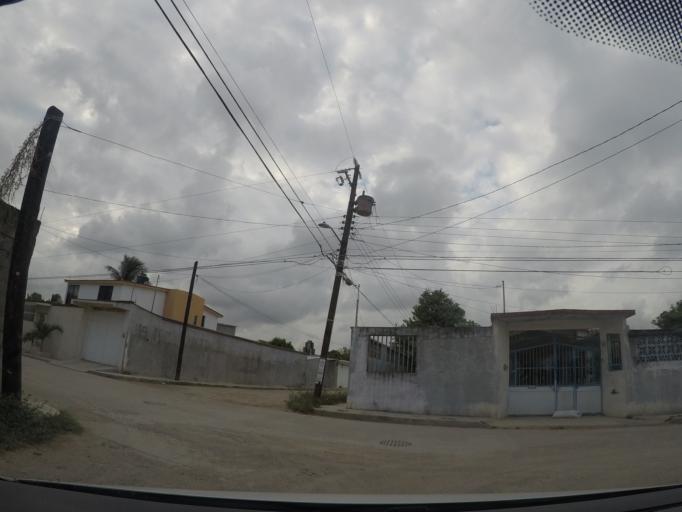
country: MX
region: Oaxaca
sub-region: Salina Cruz
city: Salina Cruz
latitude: 16.2139
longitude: -95.1997
